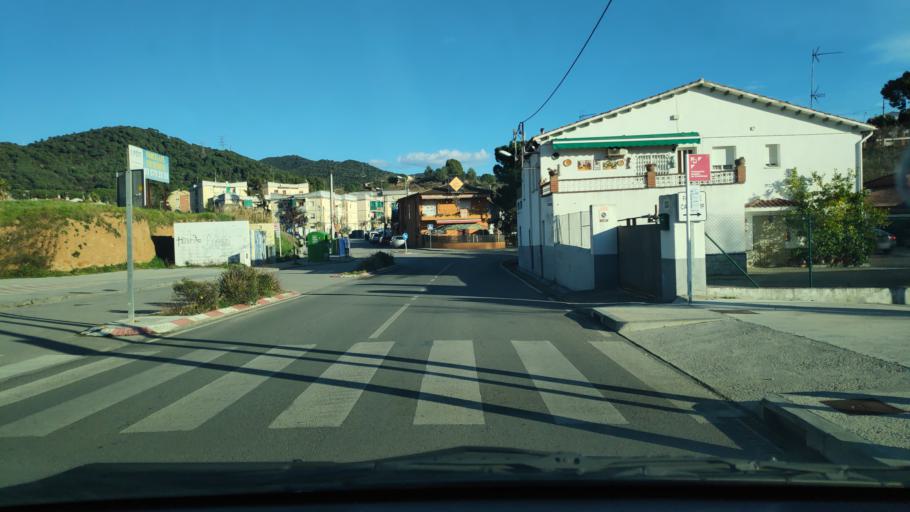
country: ES
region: Catalonia
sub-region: Provincia de Barcelona
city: Montmelo
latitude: 41.5278
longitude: 2.2406
